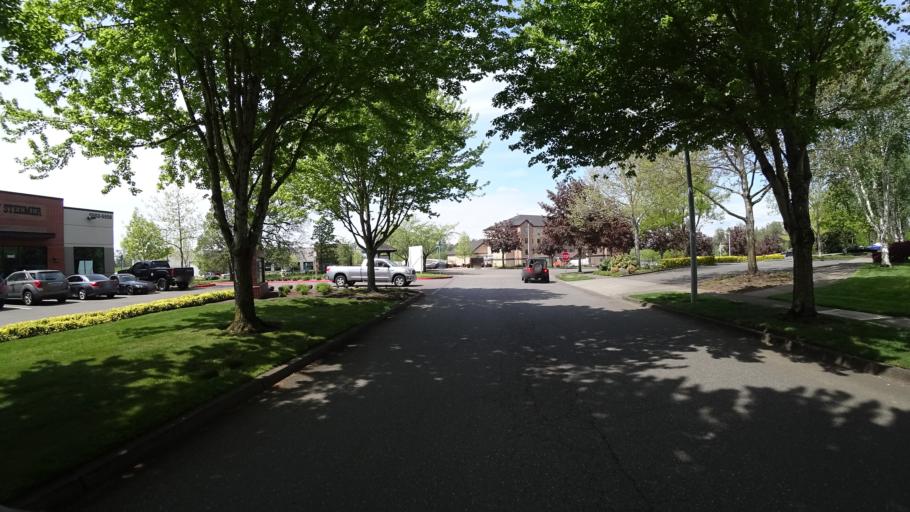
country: US
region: Oregon
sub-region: Washington County
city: Rockcreek
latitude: 45.5642
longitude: -122.9221
